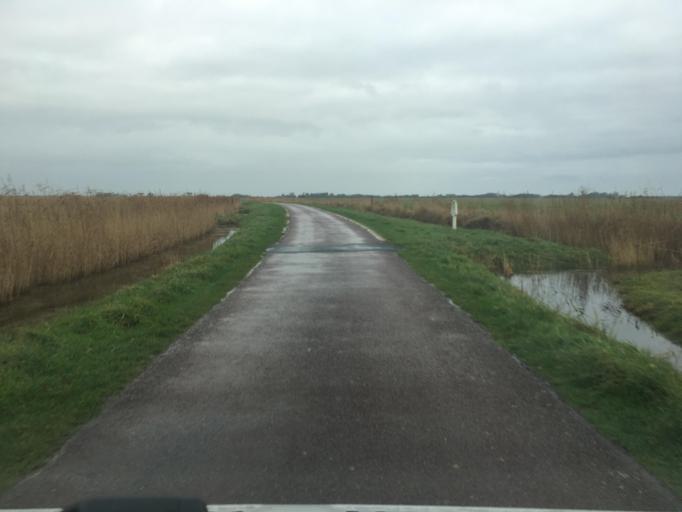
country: FR
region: Lower Normandy
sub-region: Departement de la Manche
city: Sainte-Mere-Eglise
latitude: 49.4468
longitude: -1.2357
